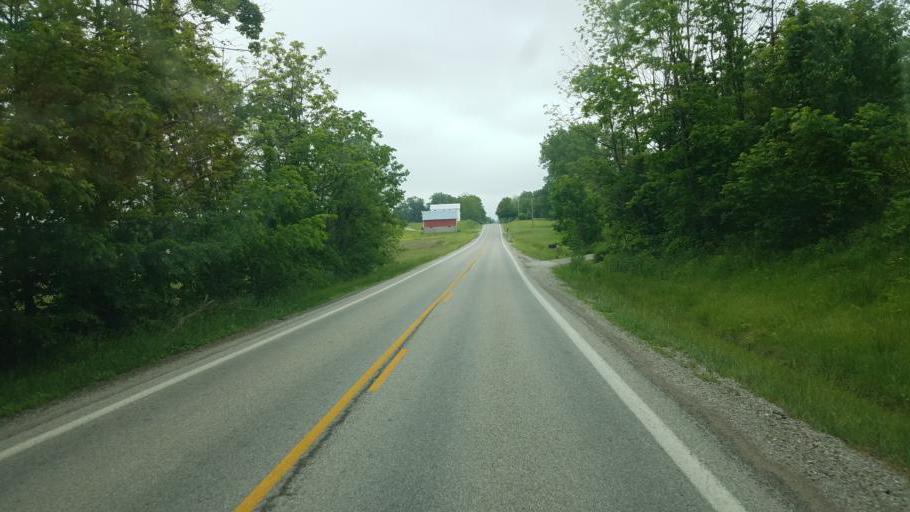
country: US
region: Ohio
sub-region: Knox County
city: Centerburg
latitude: 40.3789
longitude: -82.7281
